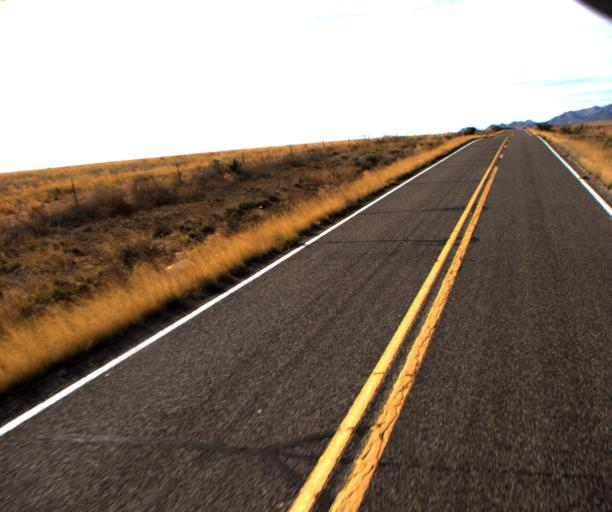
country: US
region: Arizona
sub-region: Cochise County
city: Willcox
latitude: 32.0785
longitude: -109.5192
